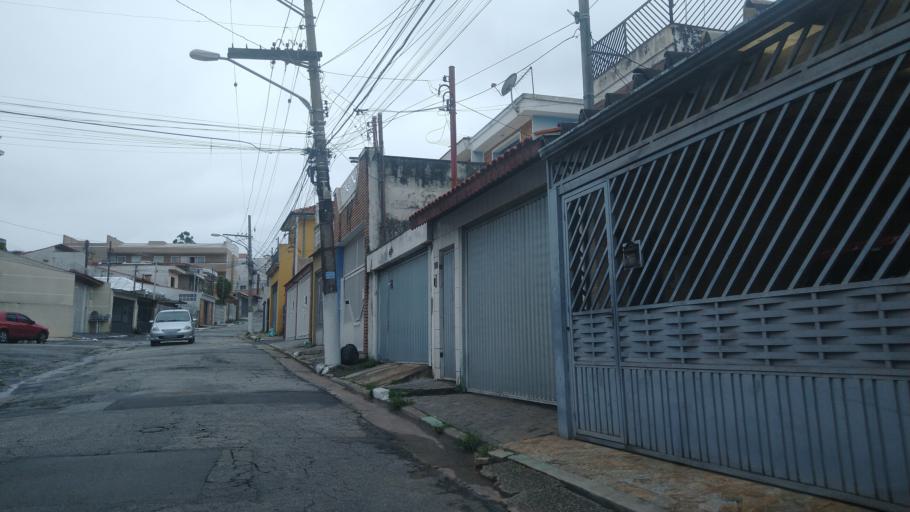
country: BR
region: Sao Paulo
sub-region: Sao Paulo
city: Sao Paulo
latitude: -23.4939
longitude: -46.6058
